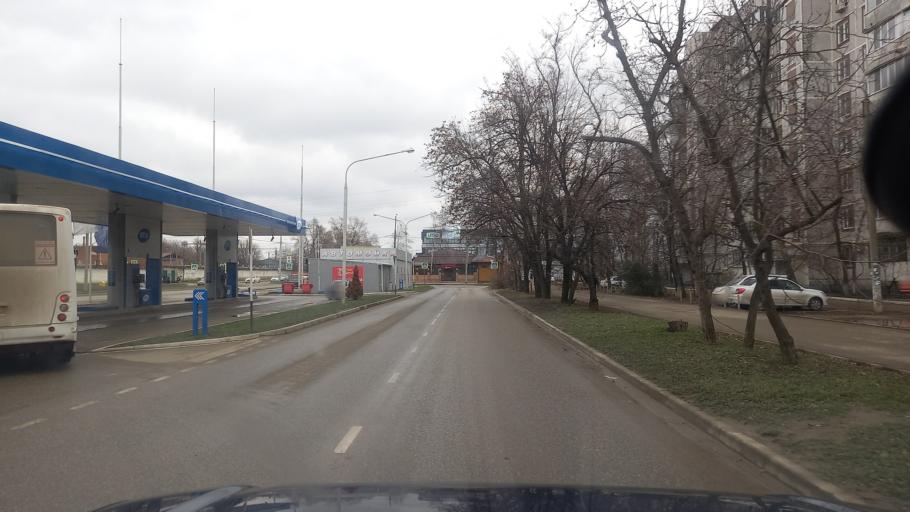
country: RU
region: Krasnodarskiy
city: Pashkovskiy
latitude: 45.0432
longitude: 39.1118
